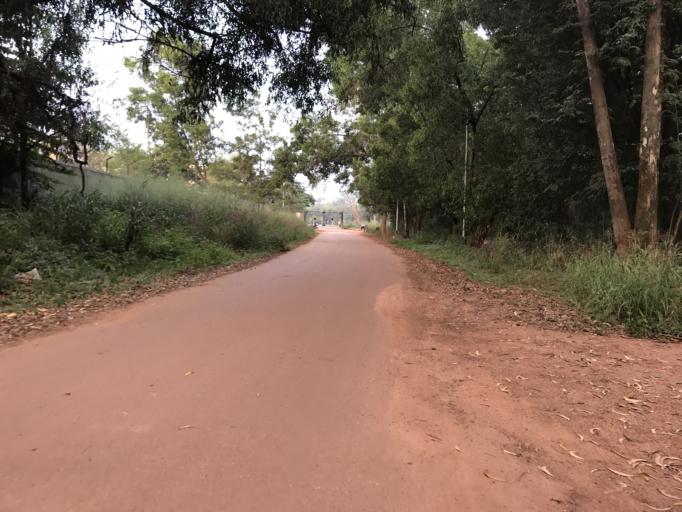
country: IN
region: Karnataka
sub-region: Bangalore Urban
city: Yelahanka
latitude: 13.0751
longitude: 77.5799
